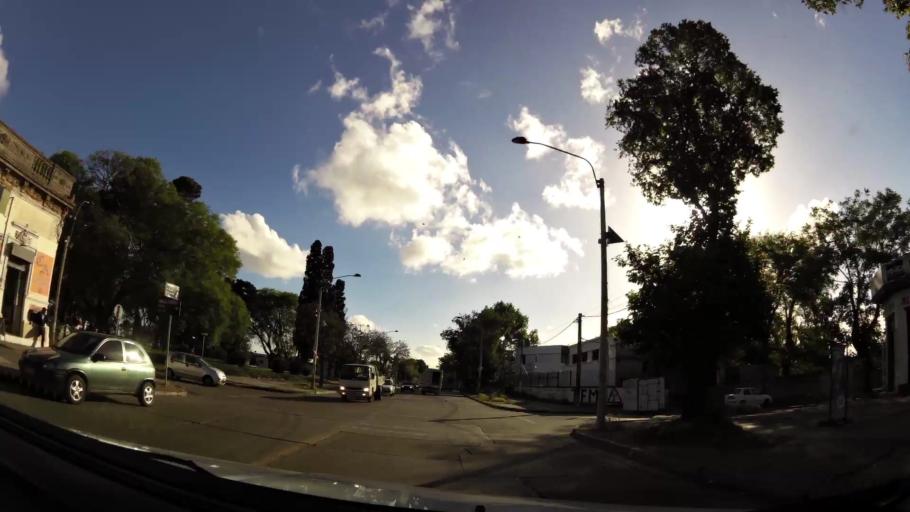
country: UY
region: Montevideo
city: Montevideo
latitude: -34.8669
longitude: -56.2371
